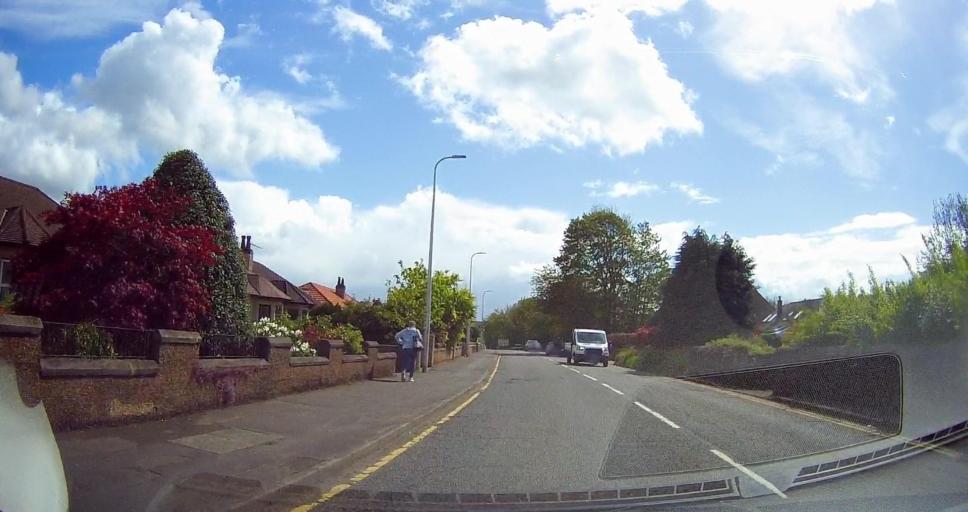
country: GB
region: Scotland
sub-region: Falkirk
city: Larbert
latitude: 56.0224
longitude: -3.8369
